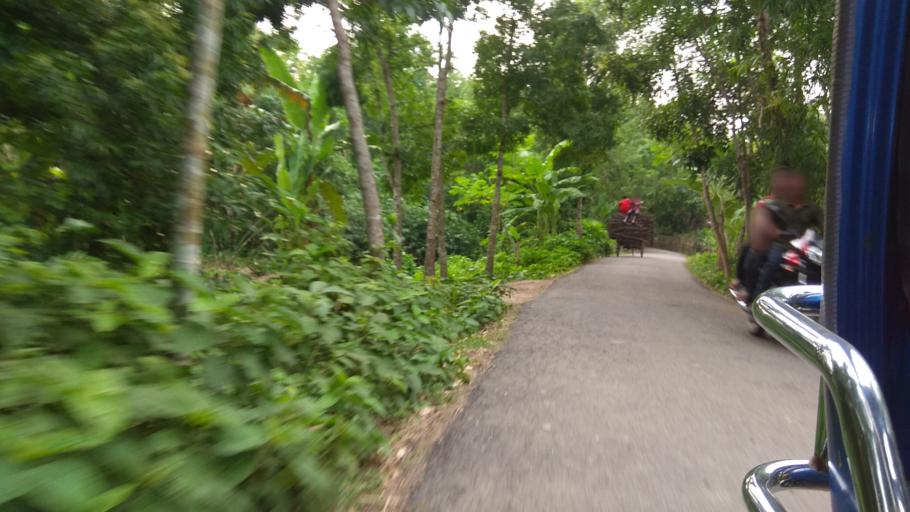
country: BD
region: Khulna
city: Kalia
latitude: 23.0379
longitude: 89.6693
